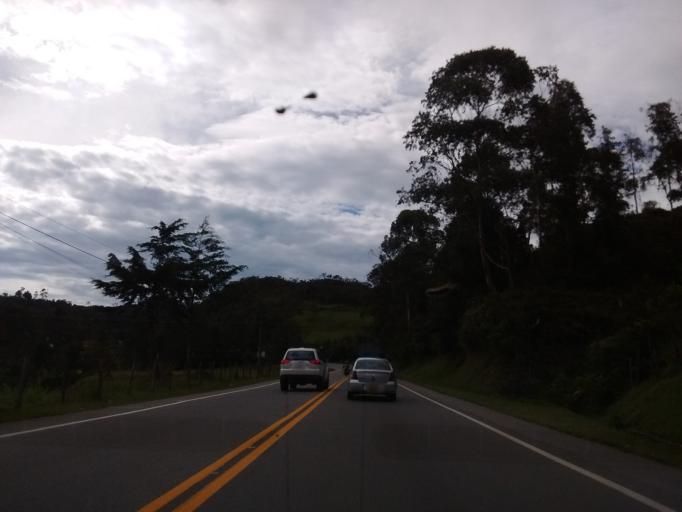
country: CO
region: Antioquia
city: Cocorna
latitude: 6.0975
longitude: -75.2238
